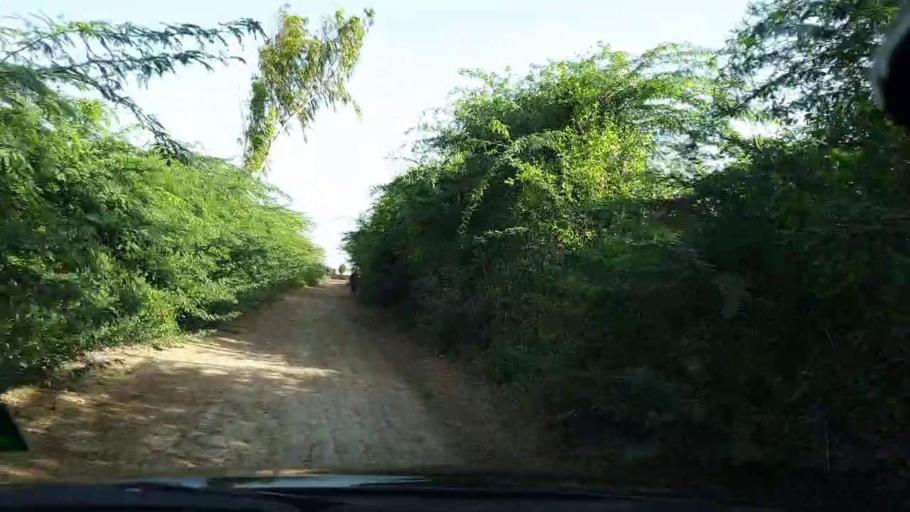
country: PK
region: Sindh
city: Tando Bago
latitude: 24.6590
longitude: 69.0421
